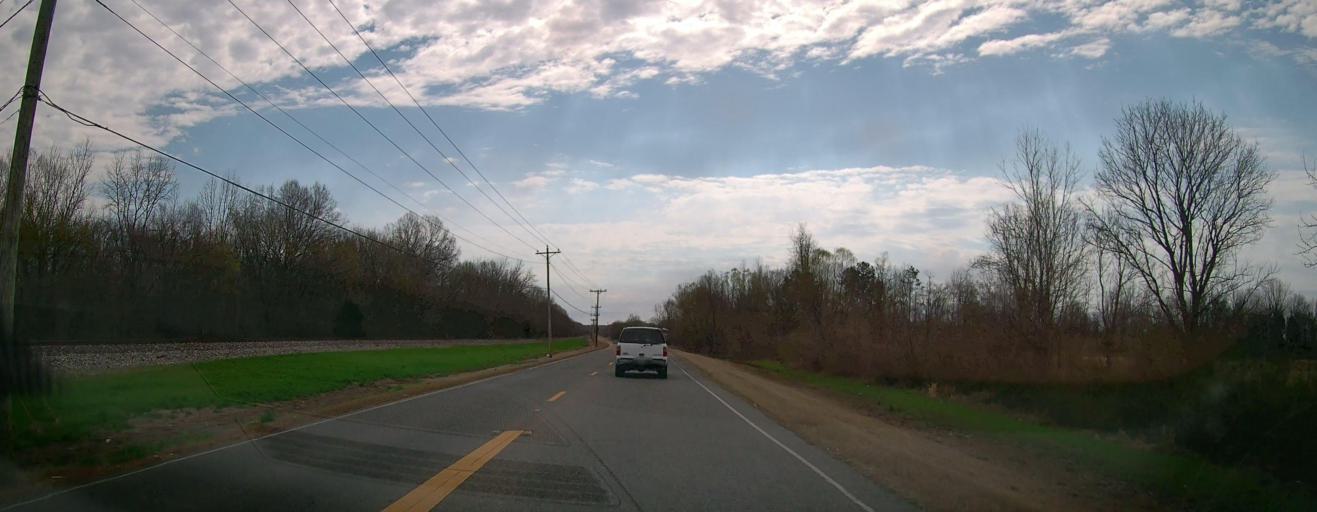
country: US
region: Mississippi
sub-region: De Soto County
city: Olive Branch
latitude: 34.9156
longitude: -89.7654
